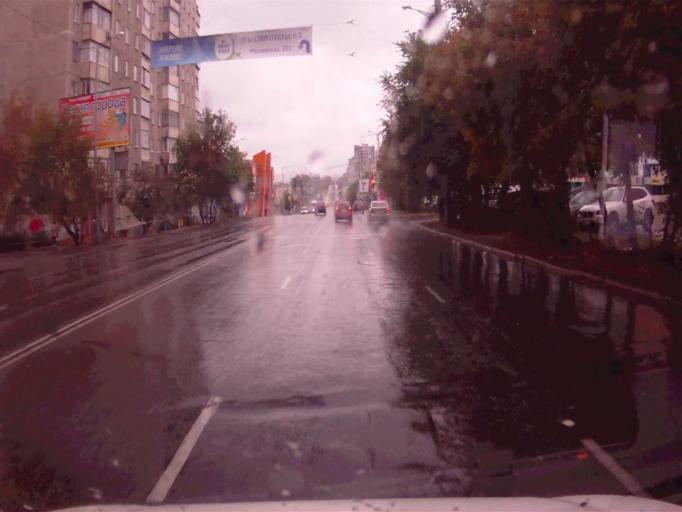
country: RU
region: Chelyabinsk
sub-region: Gorod Chelyabinsk
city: Chelyabinsk
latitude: 55.1621
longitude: 61.4163
